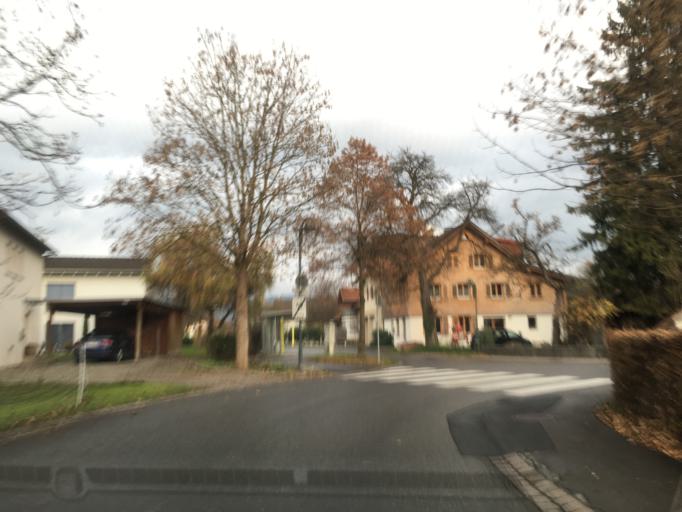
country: AT
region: Vorarlberg
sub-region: Politischer Bezirk Feldkirch
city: Mader
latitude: 47.3430
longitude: 9.6243
